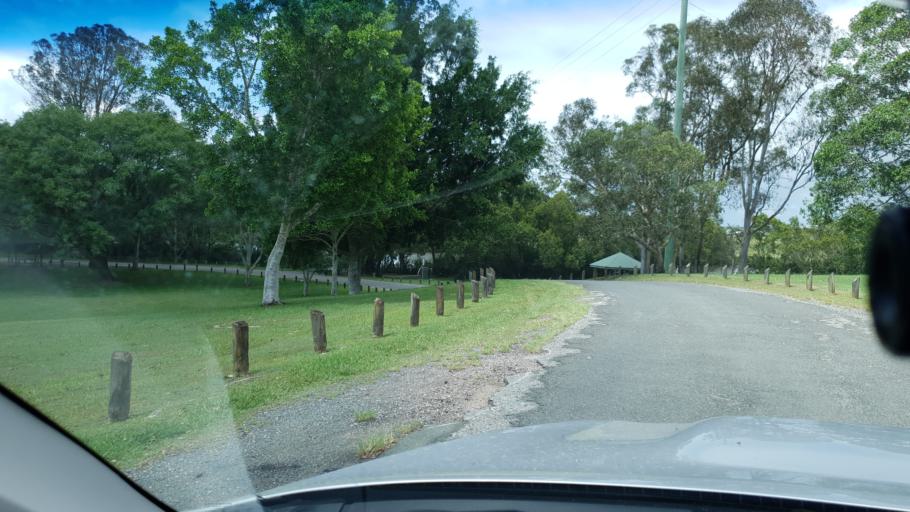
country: AU
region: Queensland
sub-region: Gold Coast
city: Yatala
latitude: -27.6795
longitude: 153.2262
